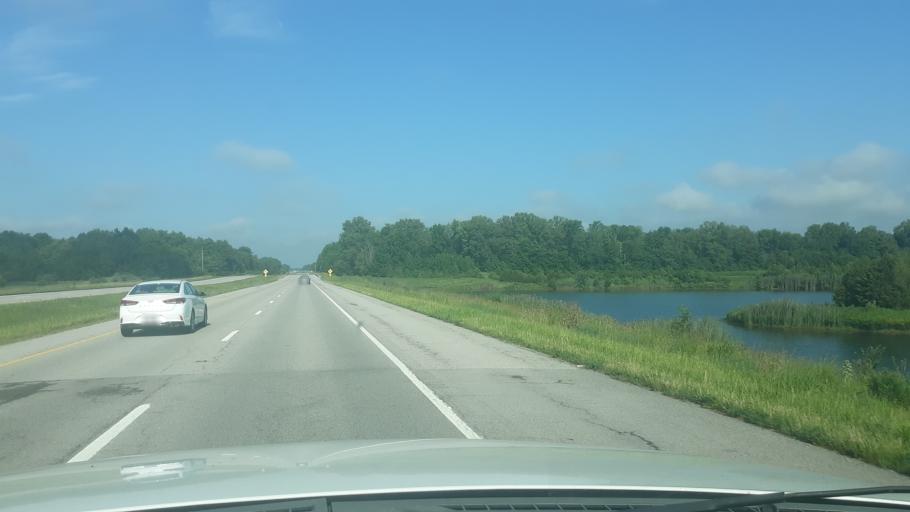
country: US
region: Illinois
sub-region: Saline County
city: Carrier Mills
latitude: 37.7334
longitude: -88.6224
